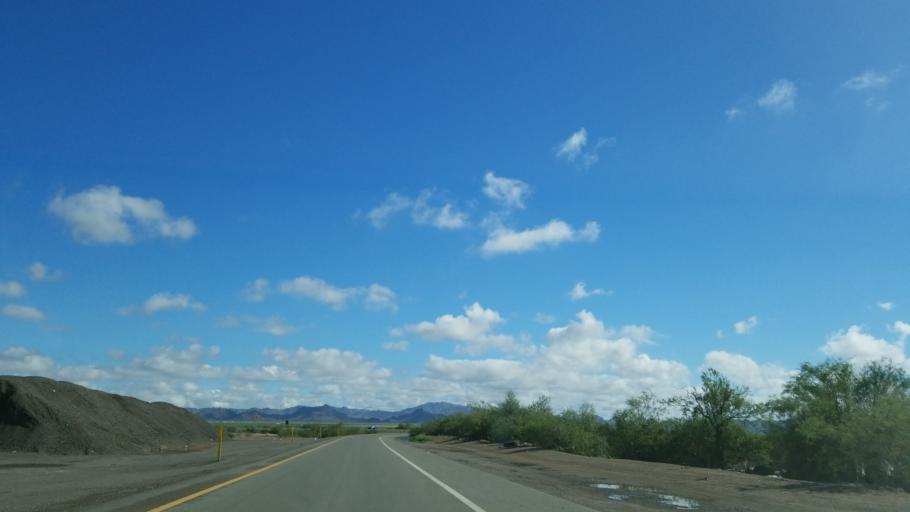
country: US
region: Arizona
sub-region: La Paz County
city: Salome
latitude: 33.6289
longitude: -113.7659
